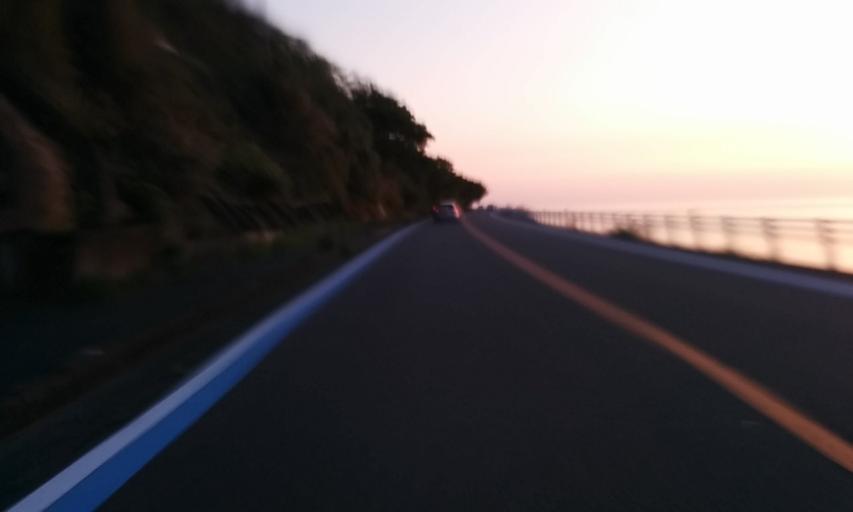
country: JP
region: Ehime
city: Ozu
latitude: 33.6461
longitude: 132.5590
